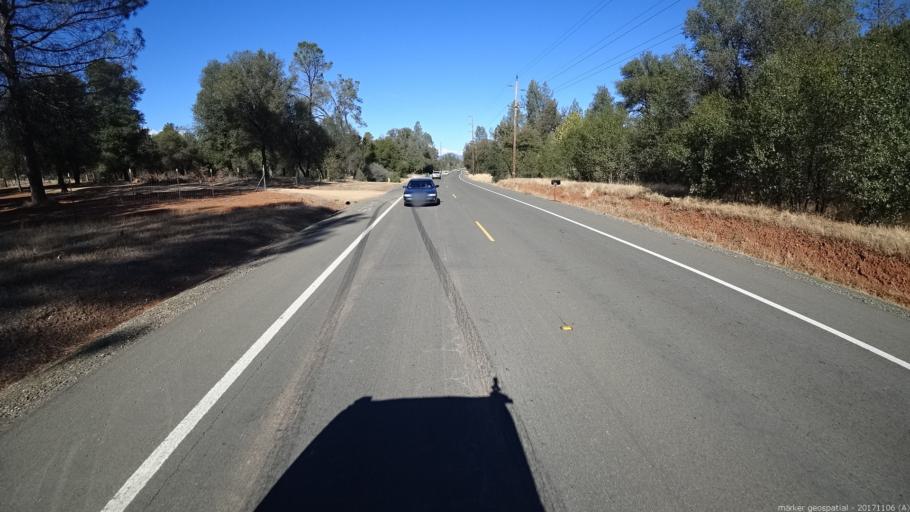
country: US
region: California
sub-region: Shasta County
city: Redding
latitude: 40.6009
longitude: -122.3135
